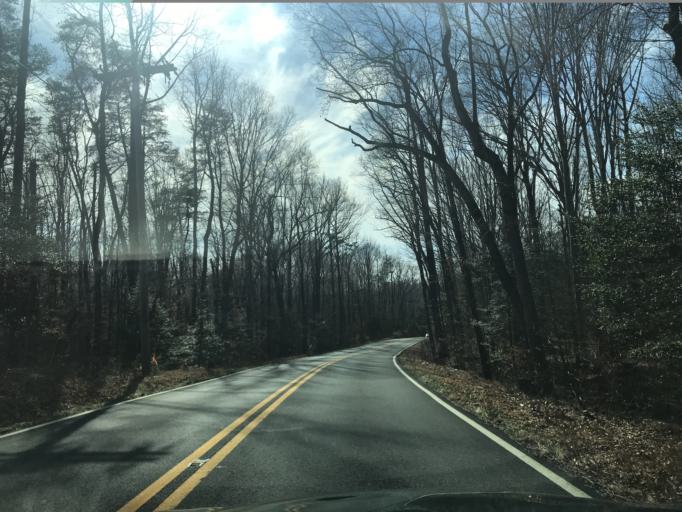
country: US
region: Maryland
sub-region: Charles County
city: Indian Head
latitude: 38.5151
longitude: -77.1458
